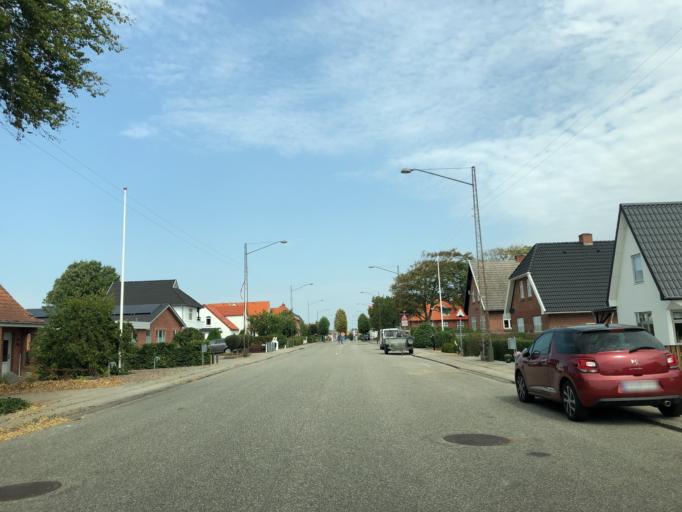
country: DK
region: Central Jutland
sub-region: Ringkobing-Skjern Kommune
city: Tarm
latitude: 55.9017
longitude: 8.5170
